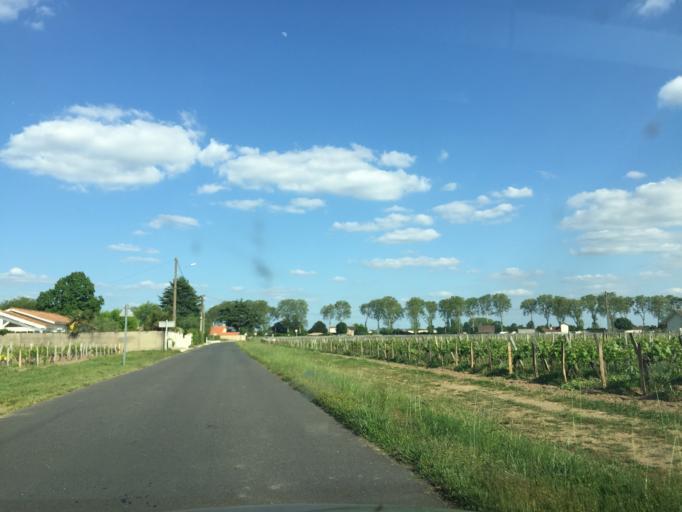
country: FR
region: Aquitaine
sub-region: Departement de la Gironde
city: Libourne
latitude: 44.9335
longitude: -0.2277
